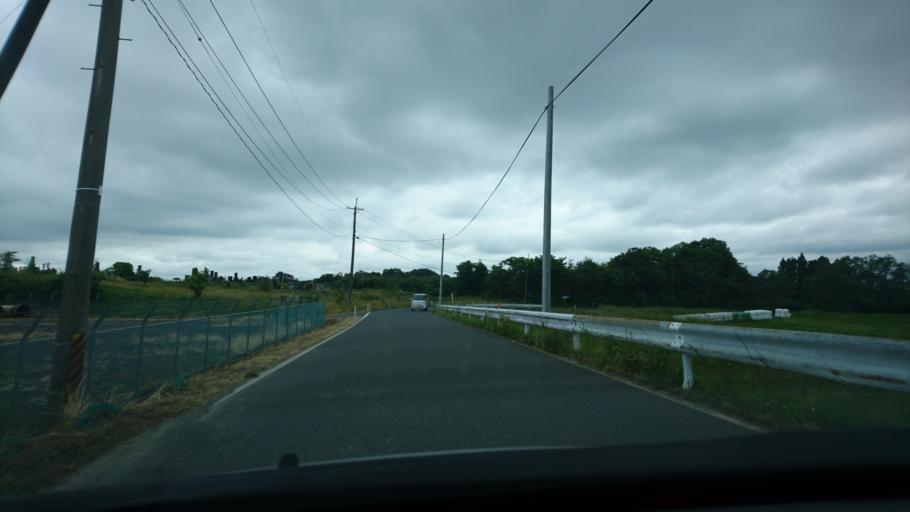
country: JP
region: Iwate
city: Ichinoseki
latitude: 38.8792
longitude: 141.2012
